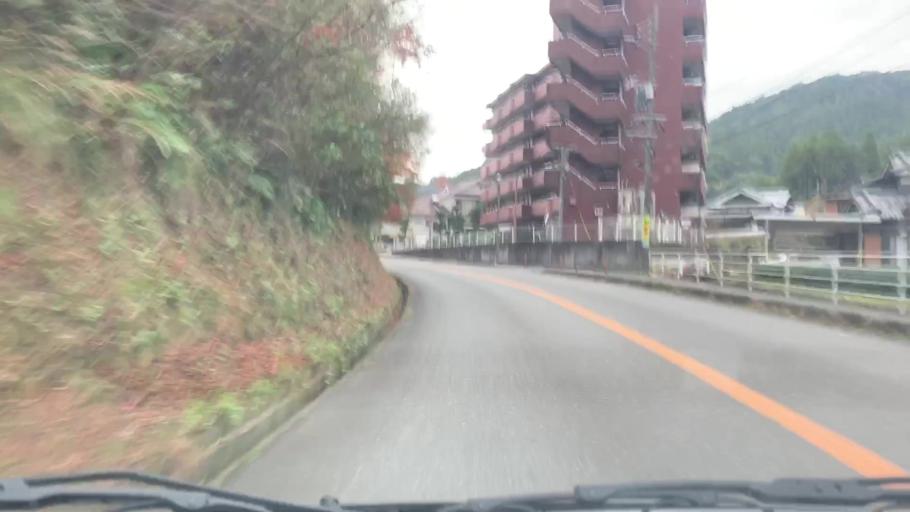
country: JP
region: Saga Prefecture
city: Ureshinomachi-shimojuku
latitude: 33.1038
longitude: 129.9783
